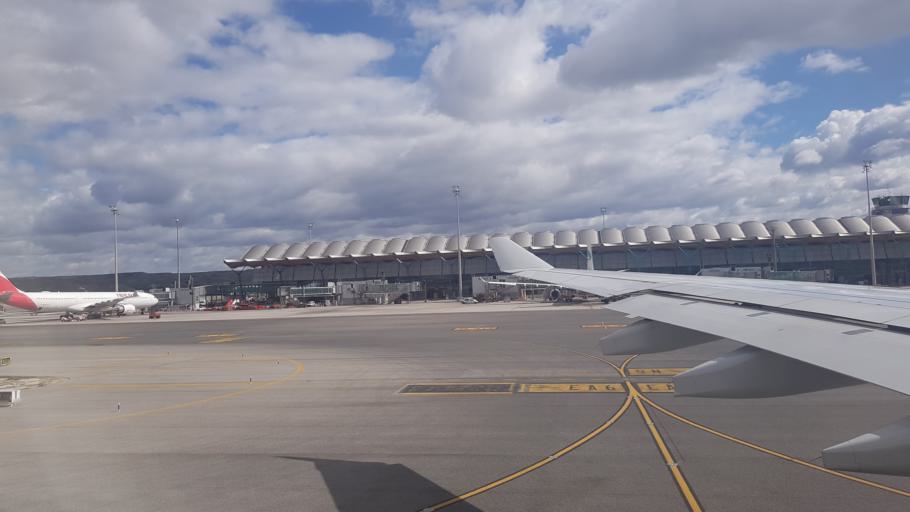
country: ES
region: Madrid
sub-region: Provincia de Madrid
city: Barajas de Madrid
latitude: 40.4975
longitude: -3.5712
